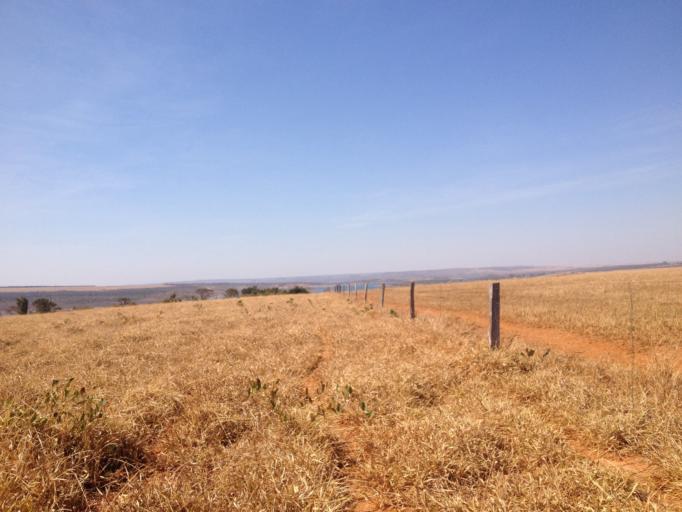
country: BR
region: Minas Gerais
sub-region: Unai
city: Unai
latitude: -16.1389
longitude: -47.3659
